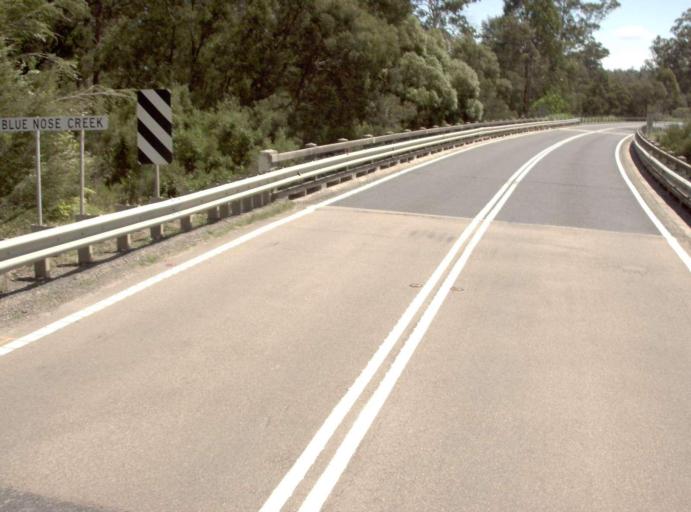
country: AU
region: New South Wales
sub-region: Bombala
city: Bombala
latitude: -37.5704
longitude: 149.1368
